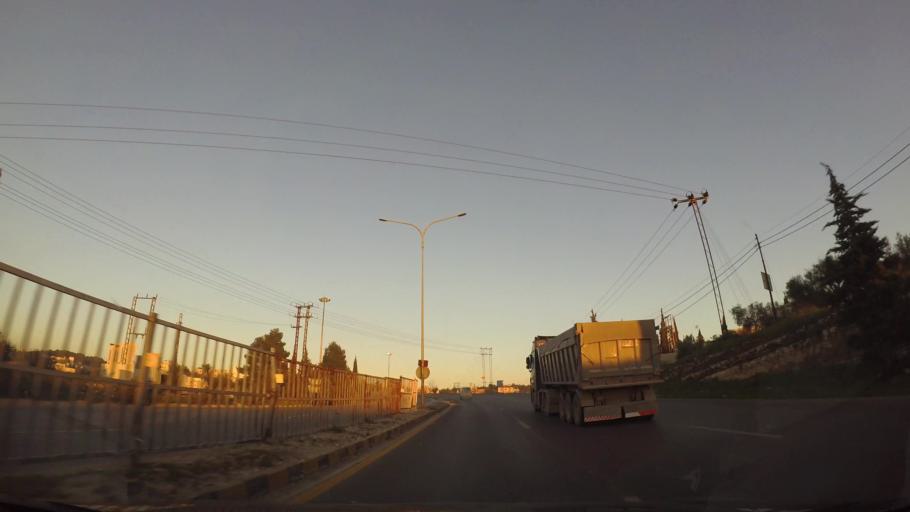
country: JO
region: Amman
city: Umm as Summaq
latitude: 31.8631
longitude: 35.8214
